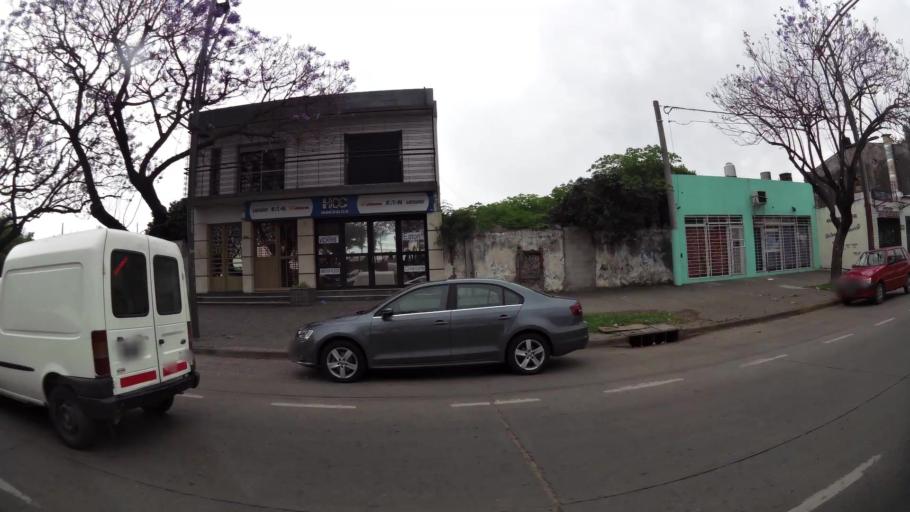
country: AR
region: Santa Fe
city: Gobernador Galvez
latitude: -32.9951
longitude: -60.6655
